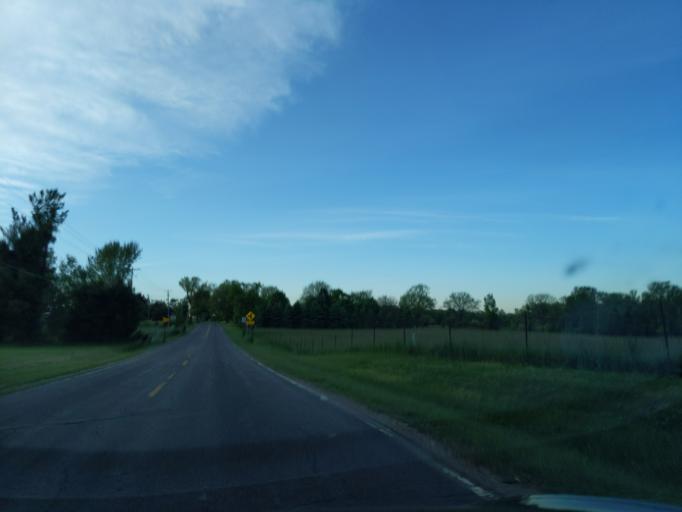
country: US
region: Michigan
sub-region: Ingham County
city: Mason
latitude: 42.5391
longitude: -84.3027
